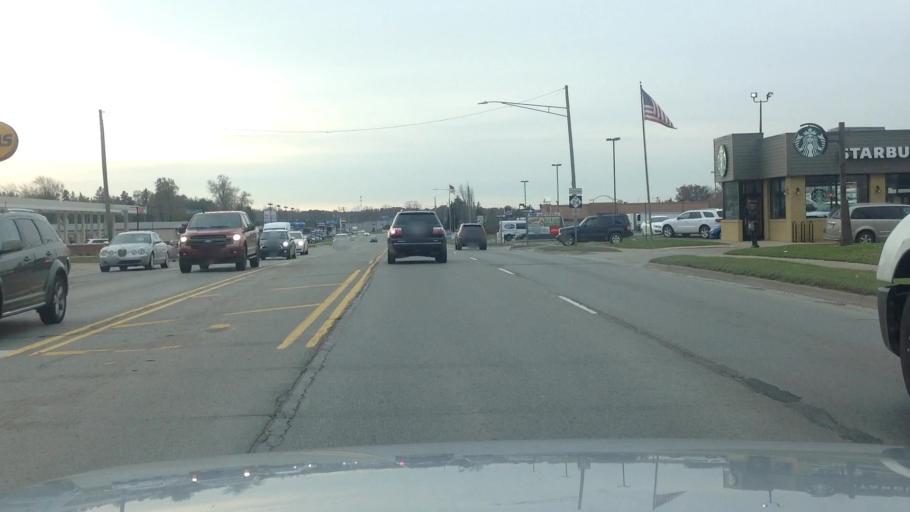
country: US
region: Michigan
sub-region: Oakland County
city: Lake Orion
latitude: 42.7757
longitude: -83.2392
